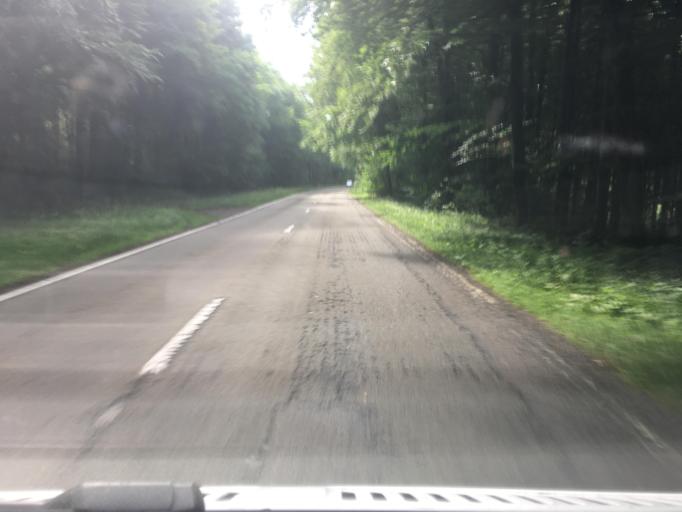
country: BE
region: Wallonia
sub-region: Province du Luxembourg
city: Florenville
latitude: 49.6470
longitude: 5.3402
